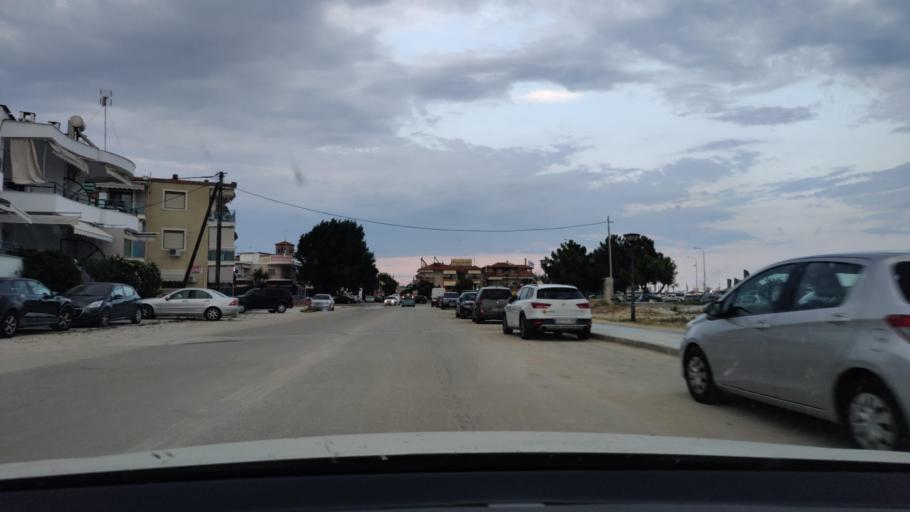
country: GR
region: East Macedonia and Thrace
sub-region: Nomos Kavalas
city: Paralia Ofryniou
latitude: 40.7661
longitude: 23.8987
